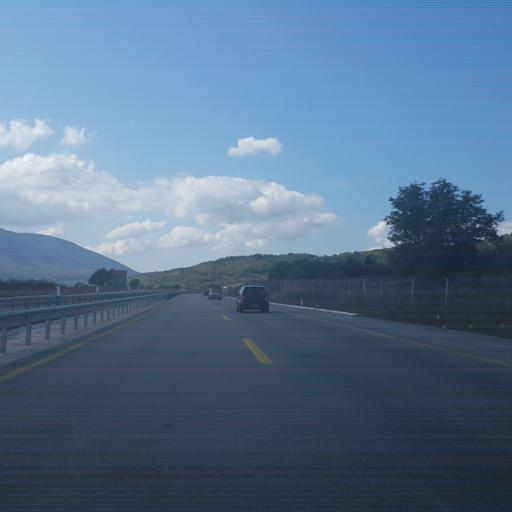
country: RS
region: Central Serbia
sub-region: Pirotski Okrug
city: Bela Palanka
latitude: 43.2368
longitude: 22.3449
